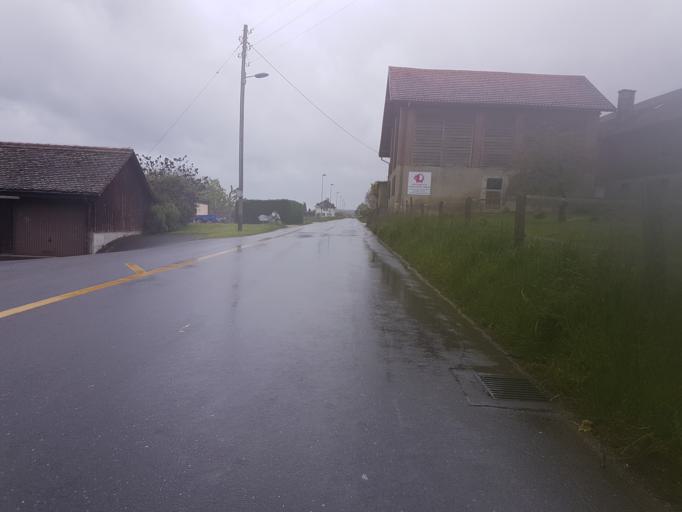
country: CH
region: Vaud
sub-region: Gros-de-Vaud District
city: Penthalaz
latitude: 46.6356
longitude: 6.5285
